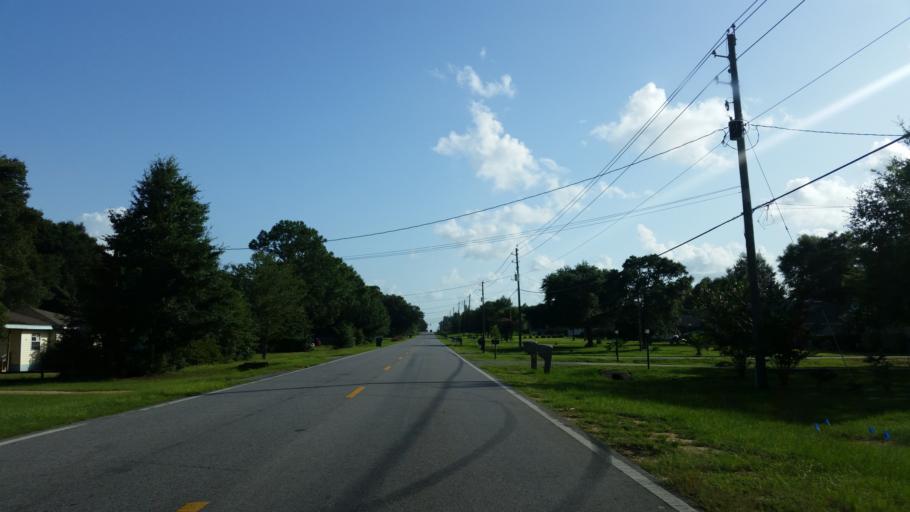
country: US
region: Florida
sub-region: Santa Rosa County
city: Bagdad
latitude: 30.5783
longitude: -87.0939
